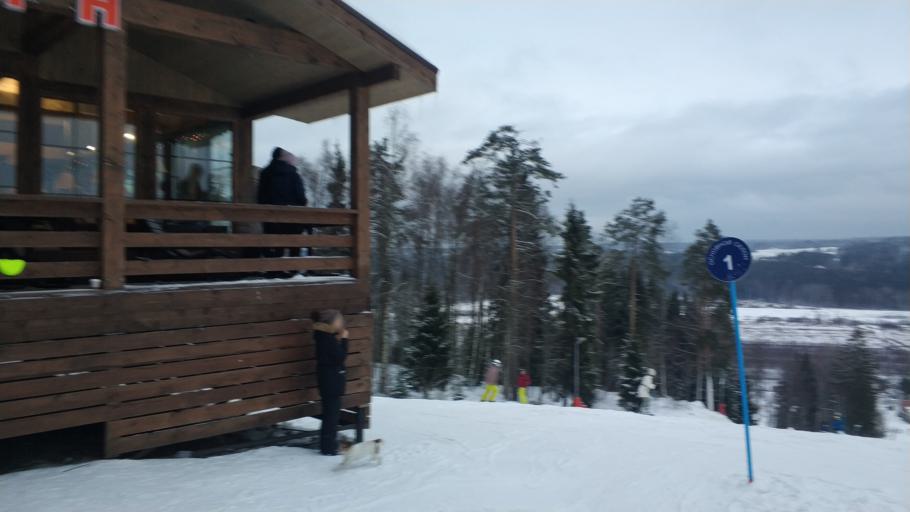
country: RU
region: Leningrad
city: Korobitsyno
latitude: 60.5238
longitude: 29.7660
